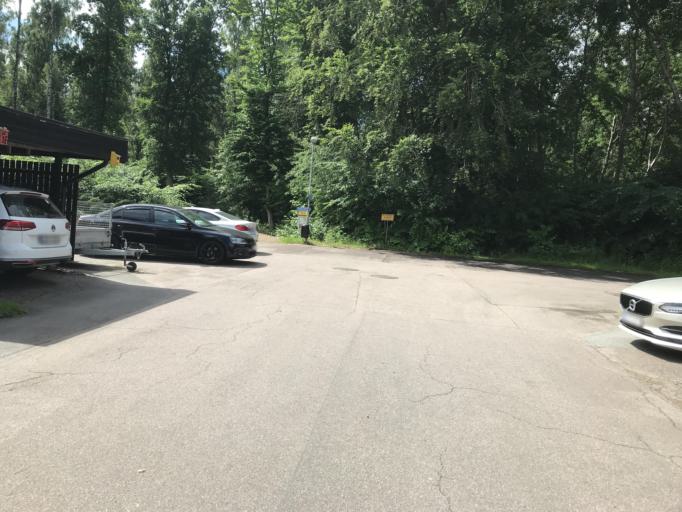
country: SE
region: Skane
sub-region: Landskrona
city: Asmundtorp
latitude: 55.8484
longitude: 12.9175
